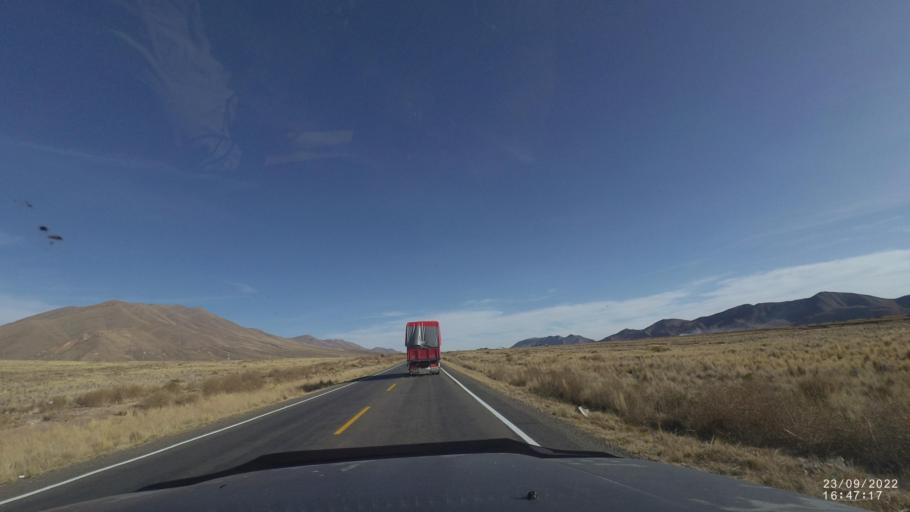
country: BO
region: Oruro
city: Poopo
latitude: -18.3664
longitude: -66.9816
